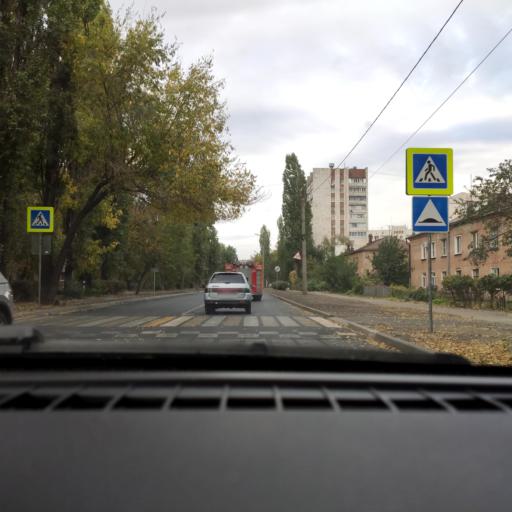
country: RU
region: Voronezj
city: Voronezh
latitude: 51.6690
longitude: 39.2548
